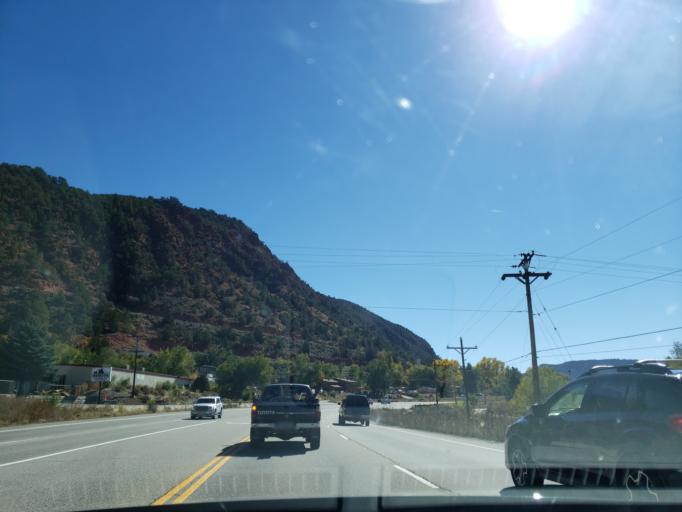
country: US
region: Colorado
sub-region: Garfield County
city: Glenwood Springs
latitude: 39.5052
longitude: -107.3024
